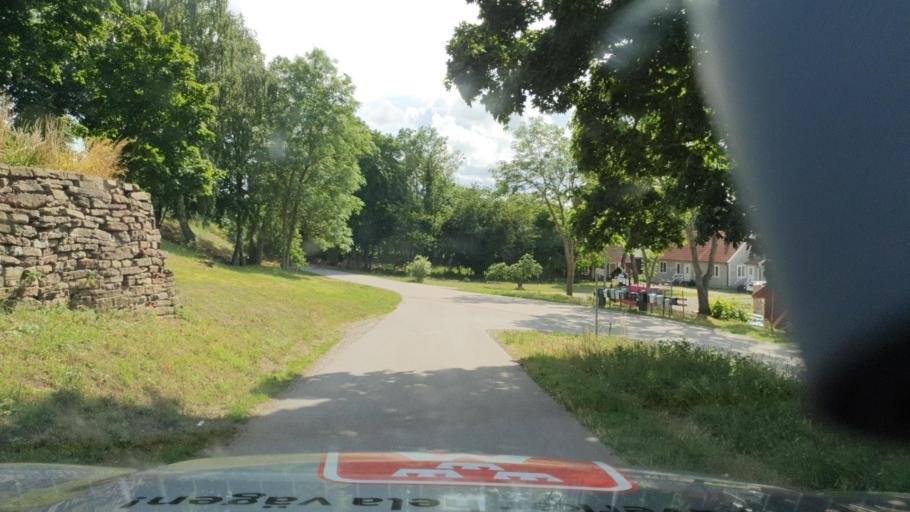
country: SE
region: Kalmar
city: Faerjestaden
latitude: 56.5963
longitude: 16.4672
